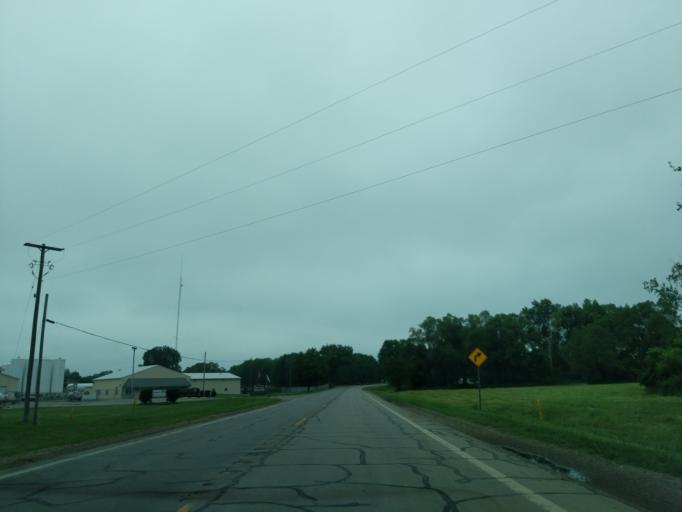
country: US
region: Michigan
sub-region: Hillsdale County
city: Litchfield
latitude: 42.0582
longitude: -84.7761
